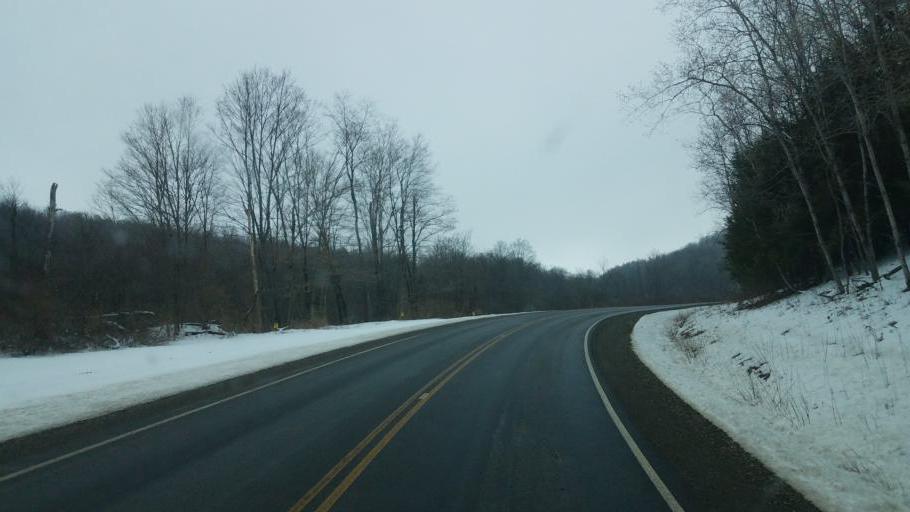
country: US
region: New York
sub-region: Allegany County
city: Andover
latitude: 42.0221
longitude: -77.7516
